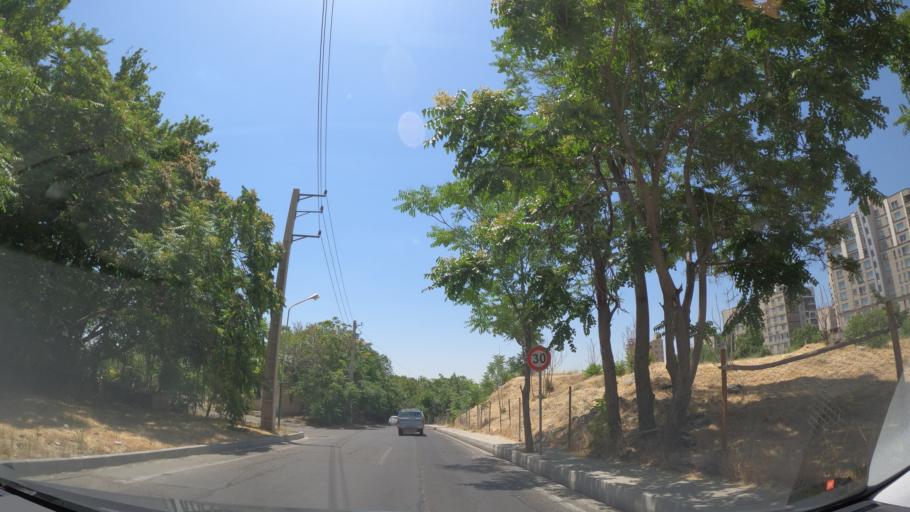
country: IR
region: Tehran
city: Tajrish
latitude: 35.7831
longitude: 51.3890
